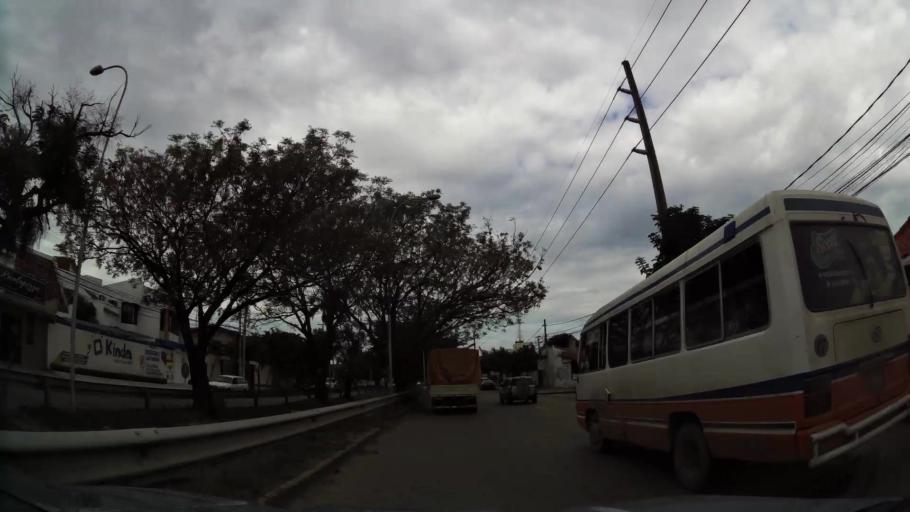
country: BO
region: Santa Cruz
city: Santa Cruz de la Sierra
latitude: -17.7559
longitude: -63.1726
